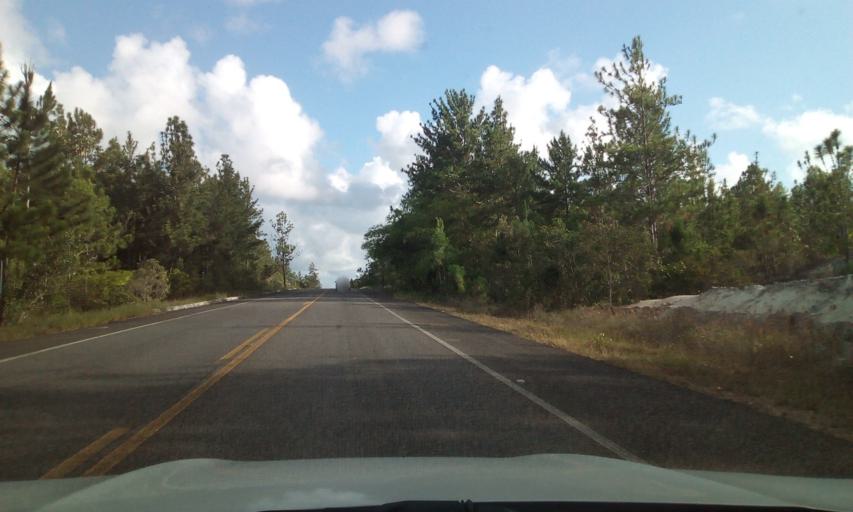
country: BR
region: Bahia
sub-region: Entre Rios
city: Entre Rios
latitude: -12.1231
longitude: -37.7894
